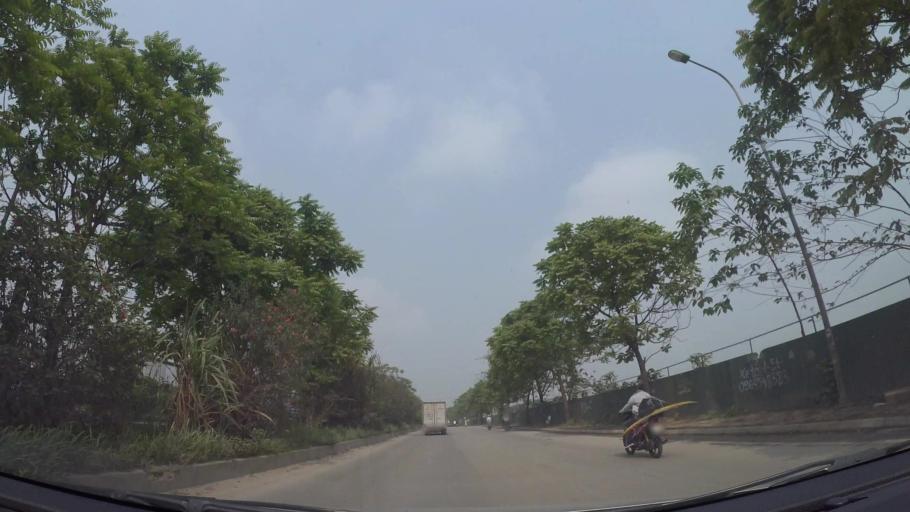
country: VN
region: Ha Noi
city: Cau Dien
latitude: 21.0106
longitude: 105.7356
